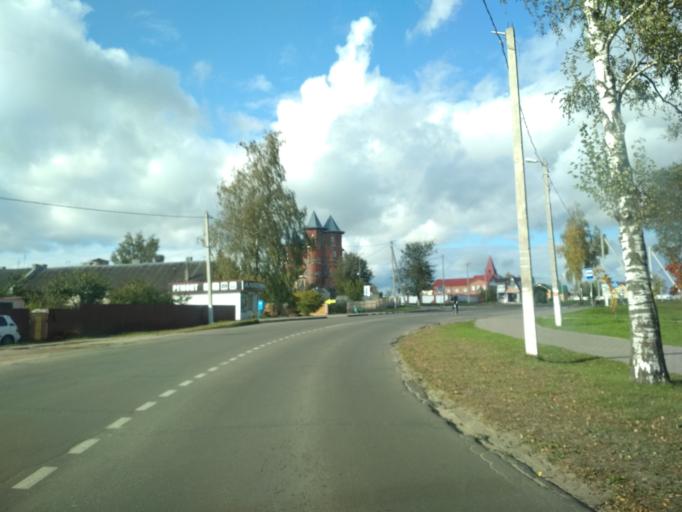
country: BY
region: Minsk
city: Mar''ina Horka
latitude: 53.5063
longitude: 28.1545
